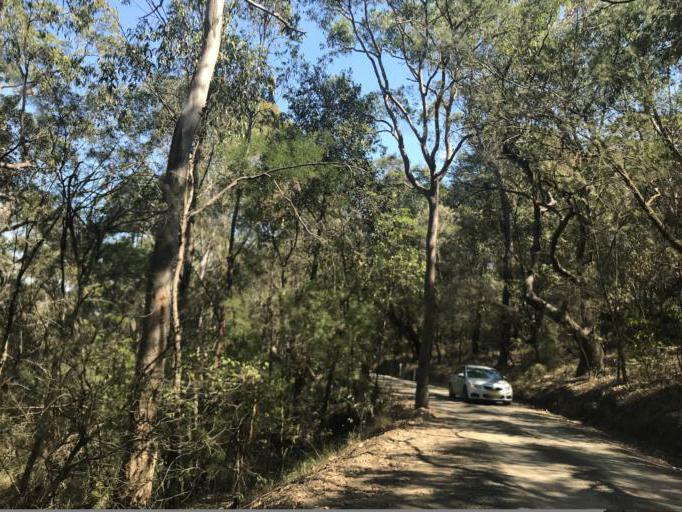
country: AU
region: New South Wales
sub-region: Hawkesbury
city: Pitt Town
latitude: -33.4103
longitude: 150.9228
